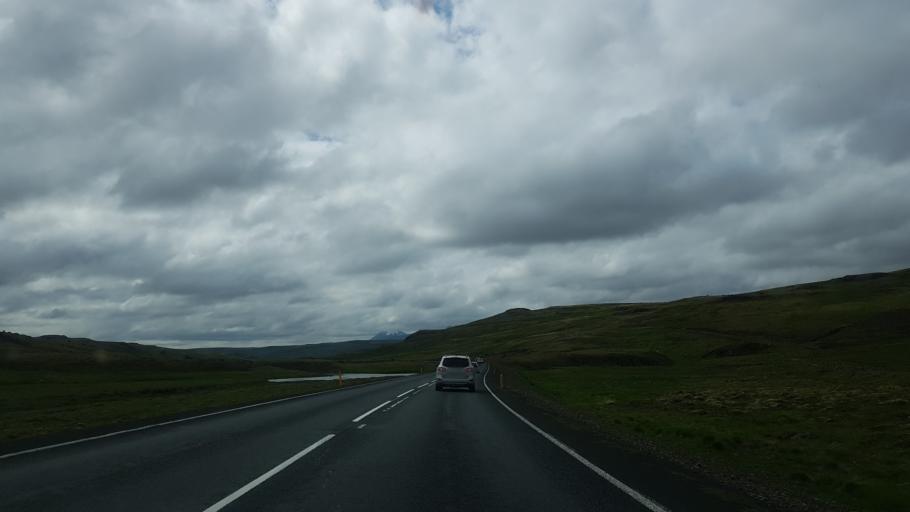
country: IS
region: West
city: Borgarnes
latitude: 64.9248
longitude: -21.1099
